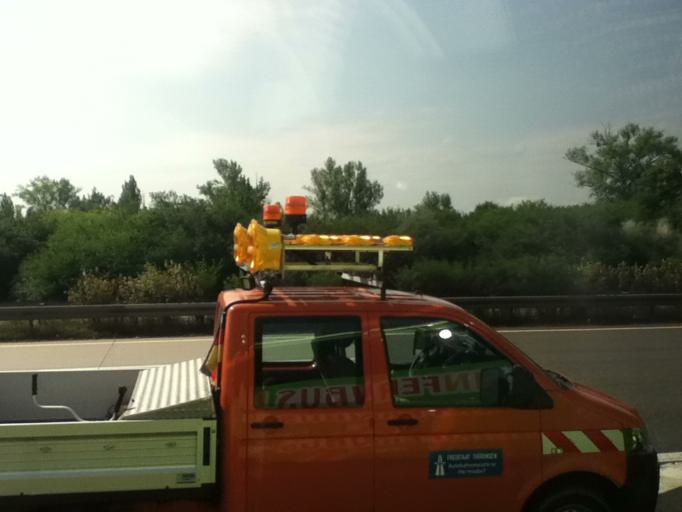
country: DE
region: Thuringia
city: Gera
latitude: 50.9100
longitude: 12.0699
